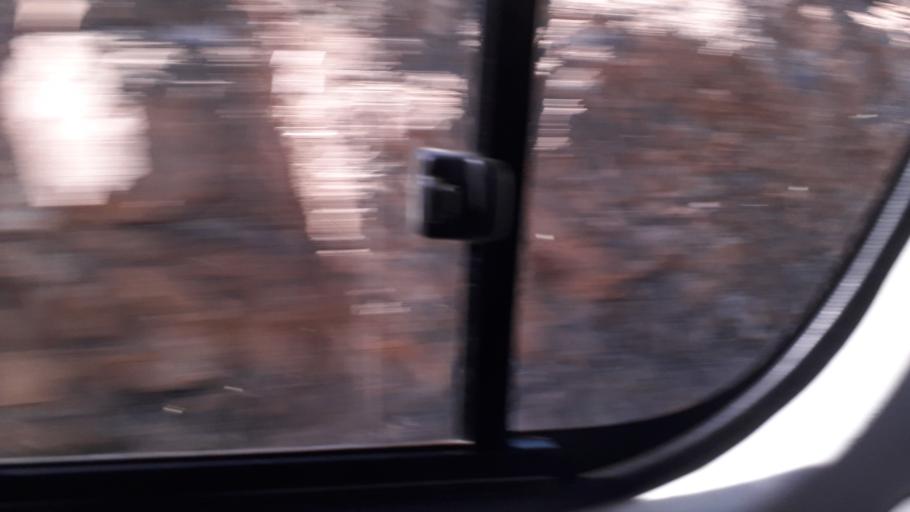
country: LS
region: Mokhotlong
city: Mokhotlong
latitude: -29.2777
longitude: 28.9342
